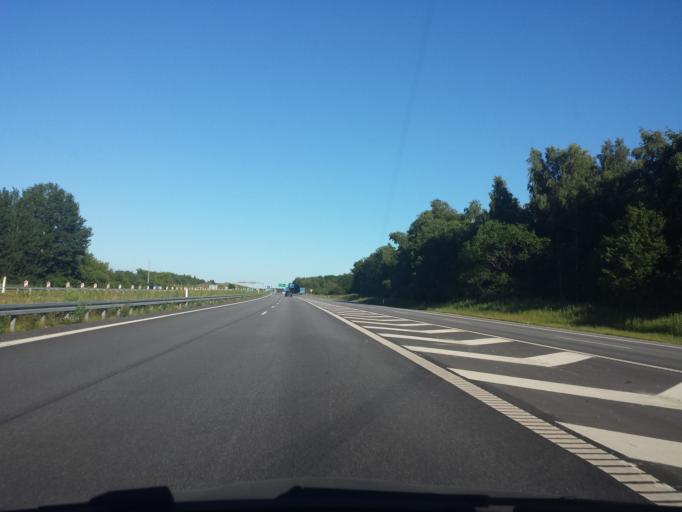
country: DK
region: Capital Region
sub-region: Ballerup Kommune
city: Ballerup
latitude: 55.7003
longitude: 12.3752
